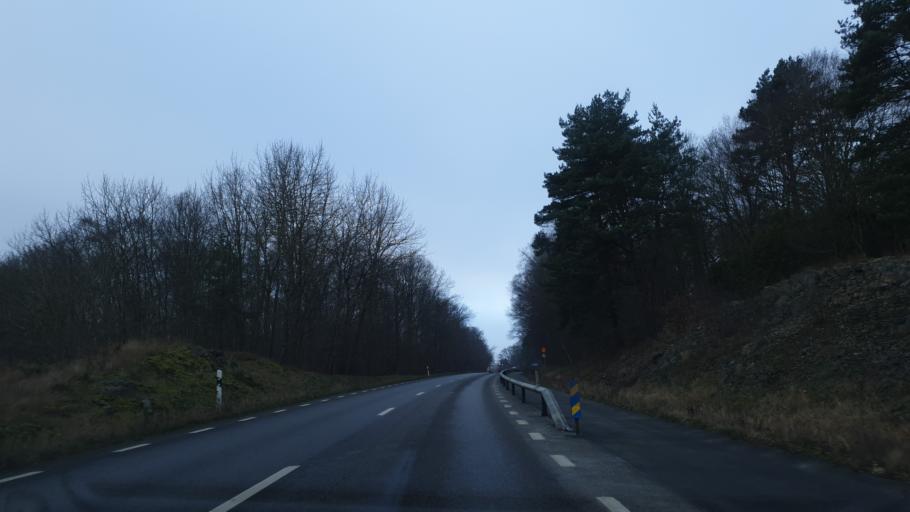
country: SE
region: Blekinge
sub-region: Solvesborgs Kommun
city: Soelvesborg
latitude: 56.0943
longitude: 14.6573
